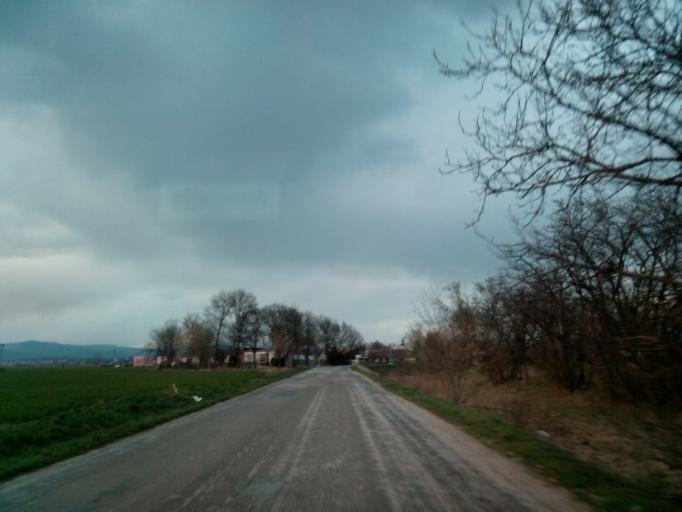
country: SK
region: Kosicky
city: Moldava nad Bodvou
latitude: 48.5848
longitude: 20.9858
